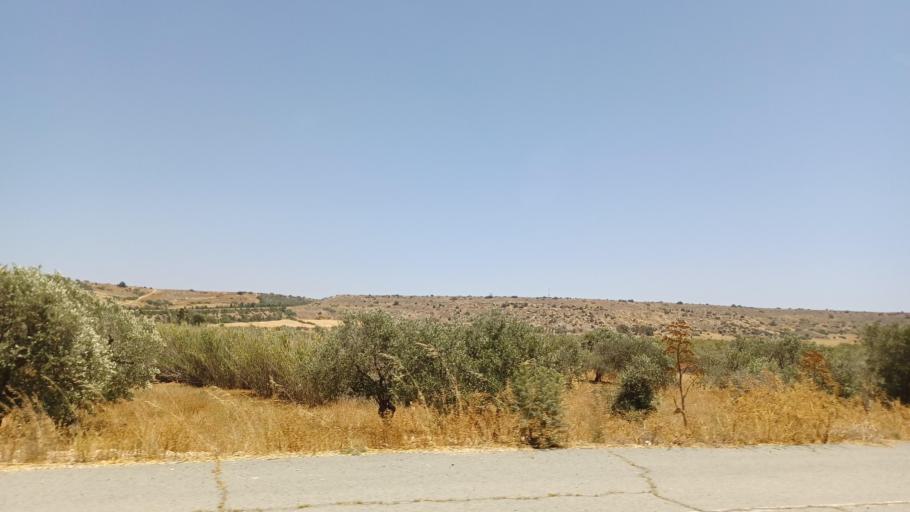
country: CY
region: Larnaka
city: Pyla
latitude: 35.0038
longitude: 33.7032
